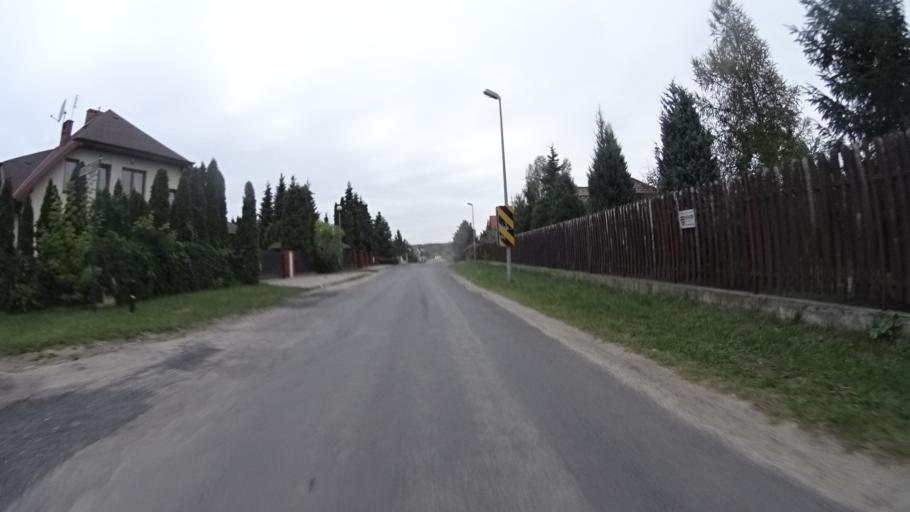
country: PL
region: Masovian Voivodeship
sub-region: Powiat warszawski zachodni
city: Stare Babice
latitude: 52.2565
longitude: 20.8211
